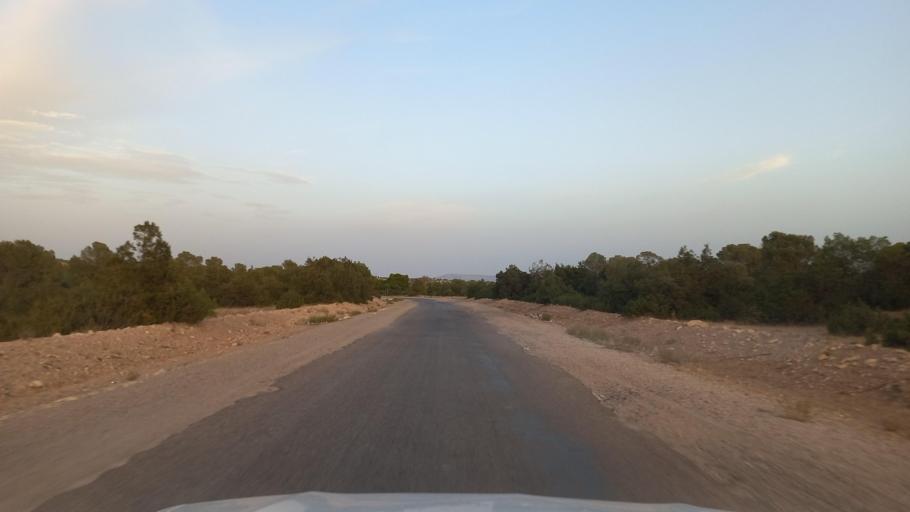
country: TN
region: Al Qasrayn
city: Sbiba
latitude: 35.4134
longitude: 8.9327
